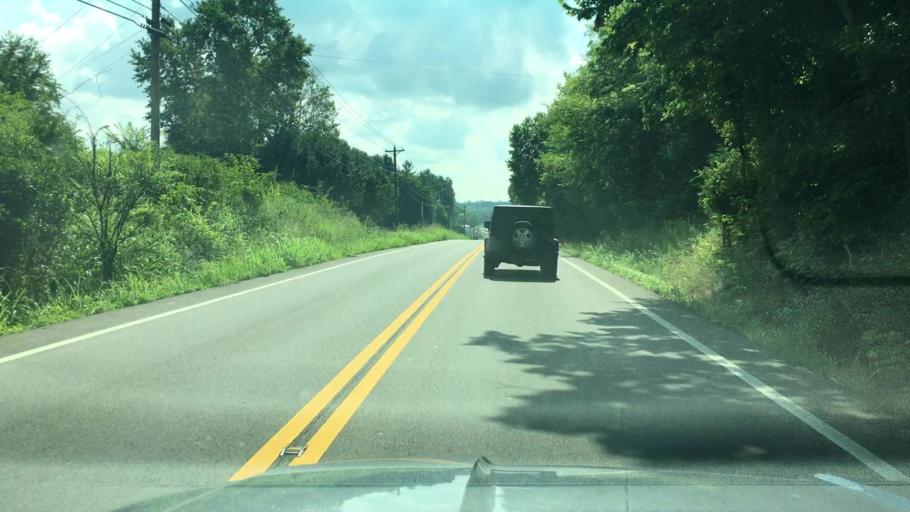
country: US
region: Tennessee
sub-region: Williamson County
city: Nolensville
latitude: 35.8687
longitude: -86.7177
